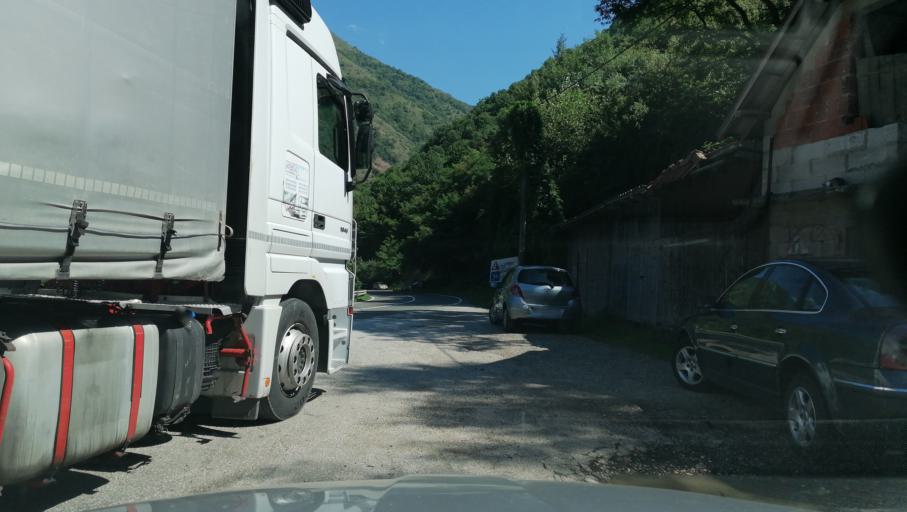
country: RS
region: Central Serbia
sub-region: Raski Okrug
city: Kraljevo
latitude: 43.6112
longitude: 20.5493
